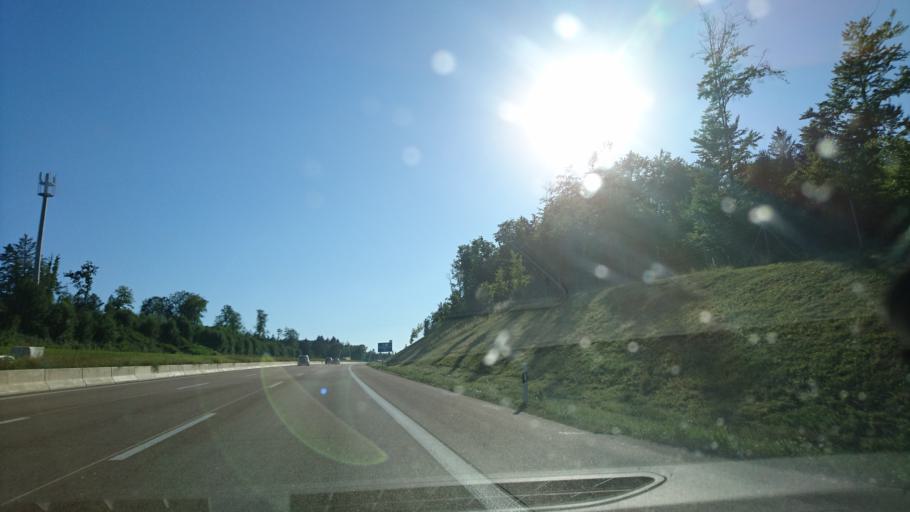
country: DE
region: Bavaria
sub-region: Swabia
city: Horgau
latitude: 48.4144
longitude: 10.6623
